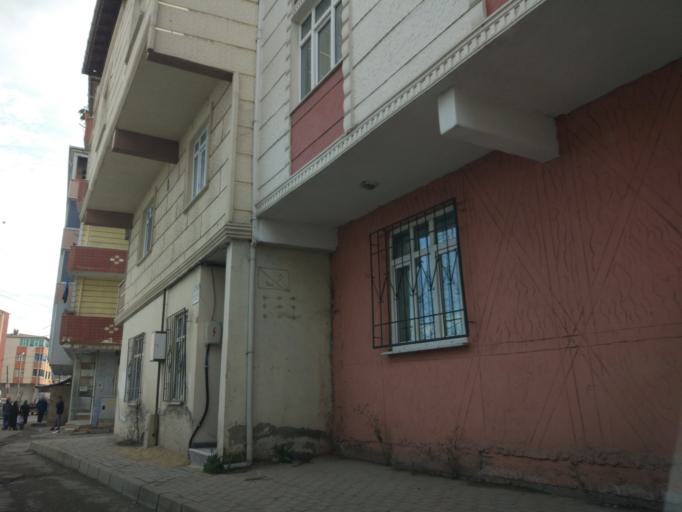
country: TR
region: Istanbul
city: Esenyurt
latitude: 41.0409
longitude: 28.7015
